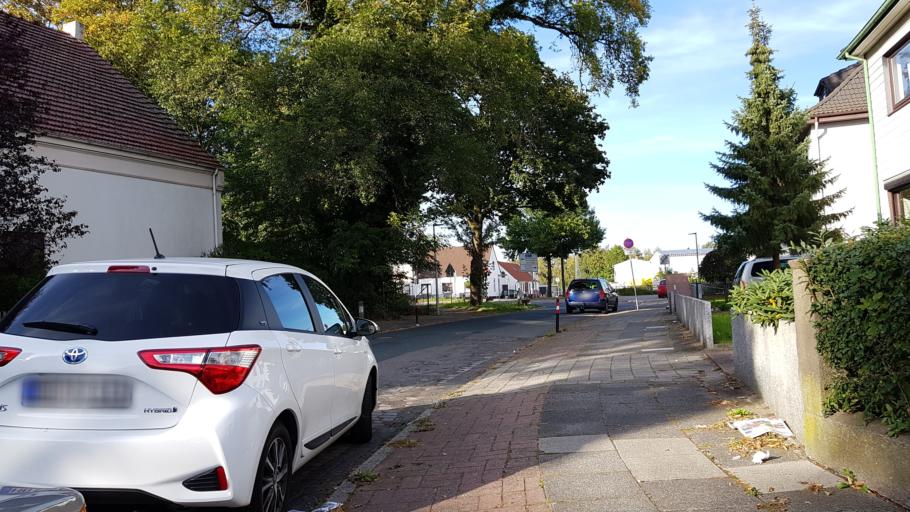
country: DE
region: Bremen
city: Bremen
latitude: 53.0498
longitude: 8.8875
